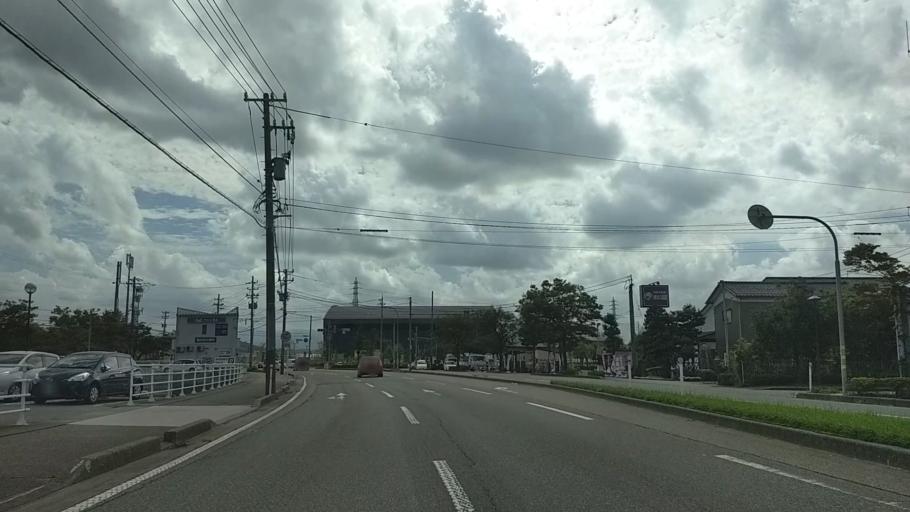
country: JP
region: Ishikawa
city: Kanazawa-shi
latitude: 36.5999
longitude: 136.6595
